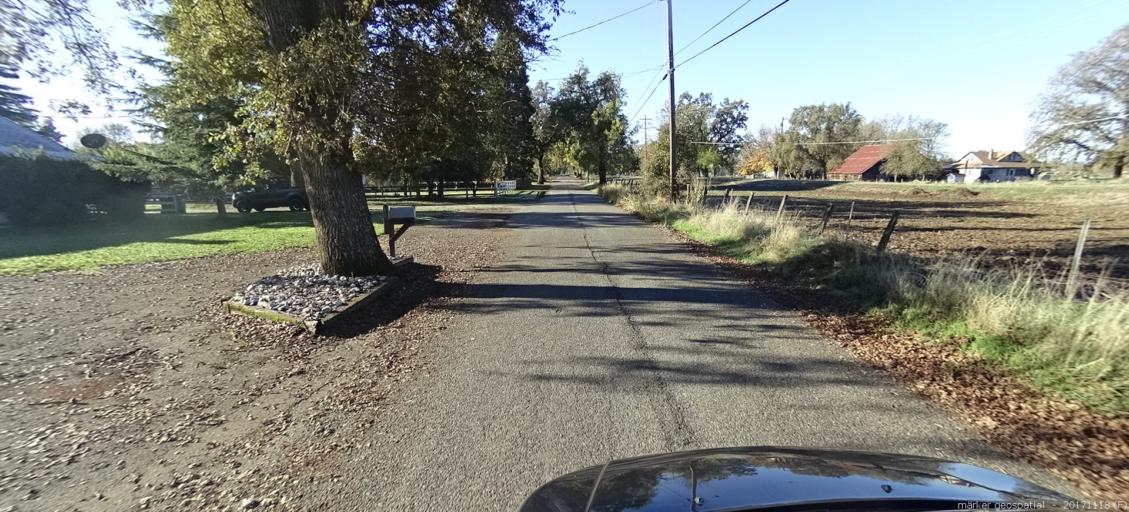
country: US
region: California
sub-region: Shasta County
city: Anderson
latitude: 40.4588
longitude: -122.2440
